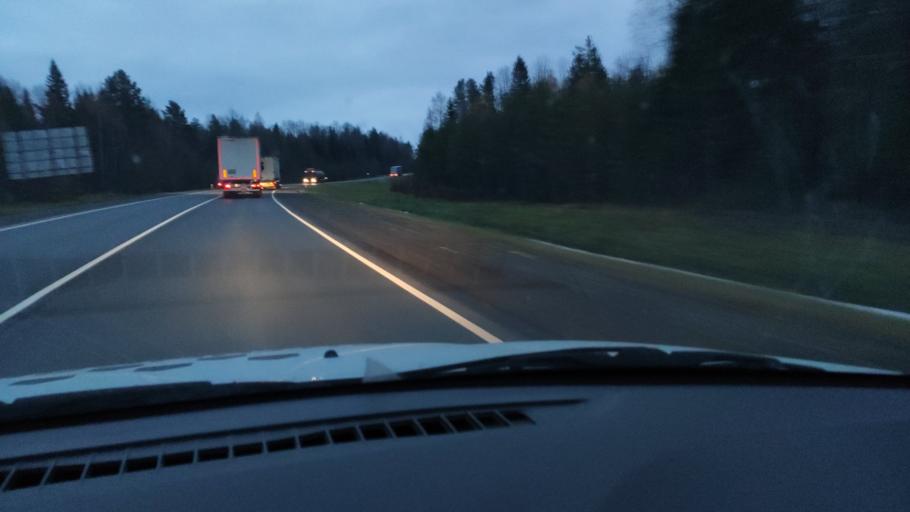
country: RU
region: Kirov
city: Kostino
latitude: 58.8306
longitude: 53.4074
